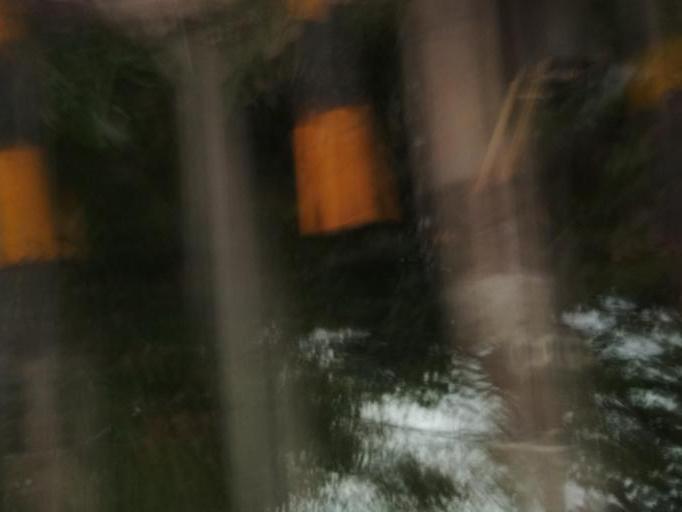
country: ID
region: West Java
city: Caringin
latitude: -6.7135
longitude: 106.8204
